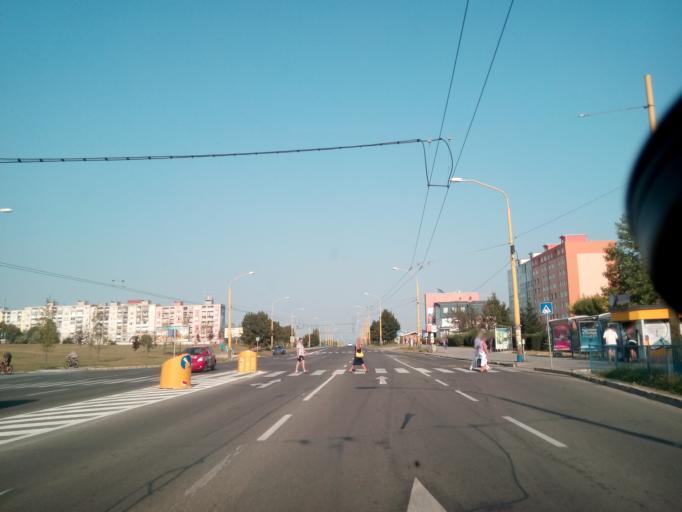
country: SK
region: Kosicky
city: Kosice
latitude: 48.7115
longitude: 21.2122
